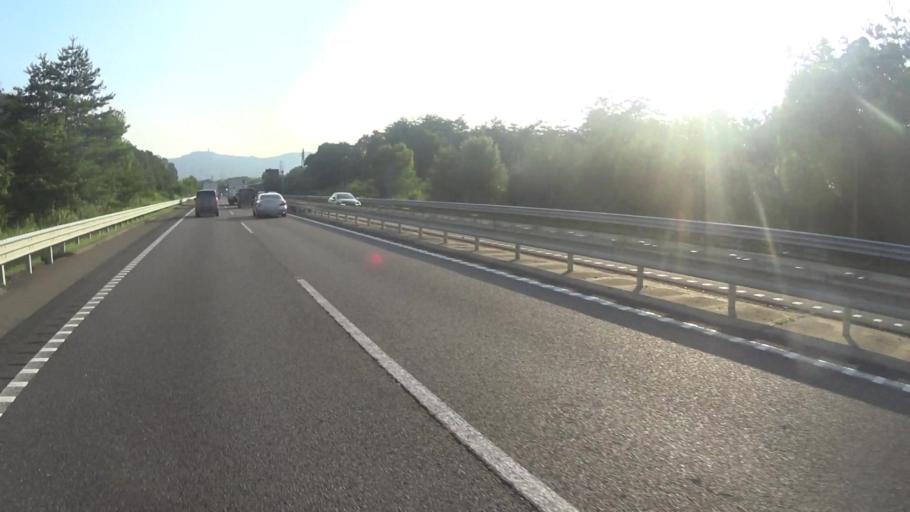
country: JP
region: Shiga Prefecture
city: Otsu-shi
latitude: 34.9646
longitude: 135.9221
